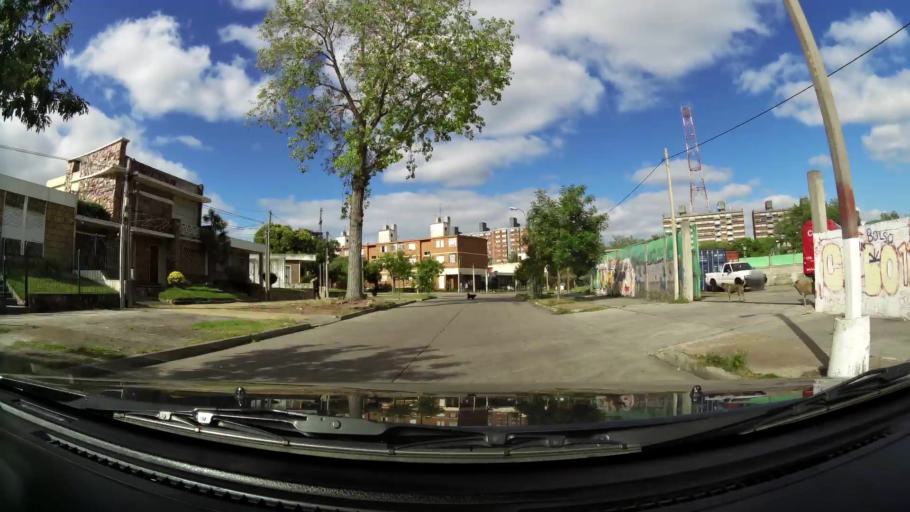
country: UY
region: Montevideo
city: Montevideo
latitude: -34.8787
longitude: -56.1633
